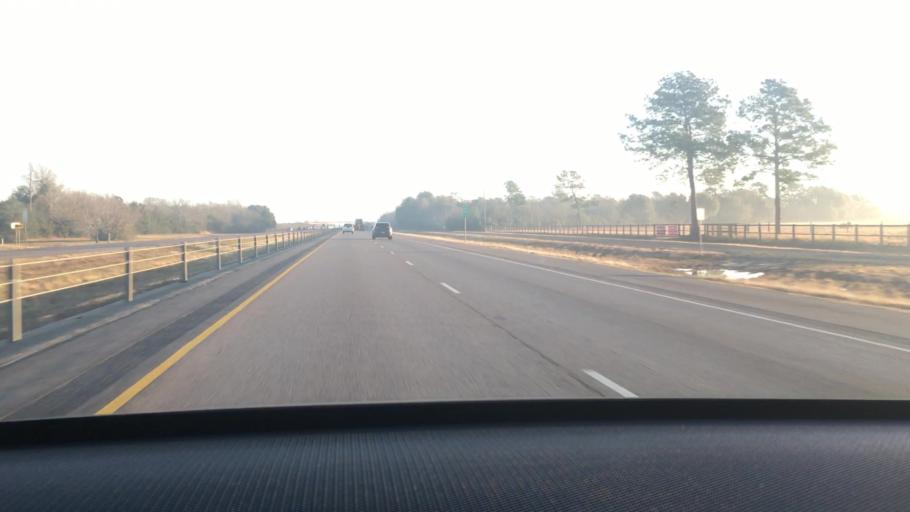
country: US
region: Texas
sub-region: Jefferson County
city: Fannett
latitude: 29.9547
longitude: -94.2413
